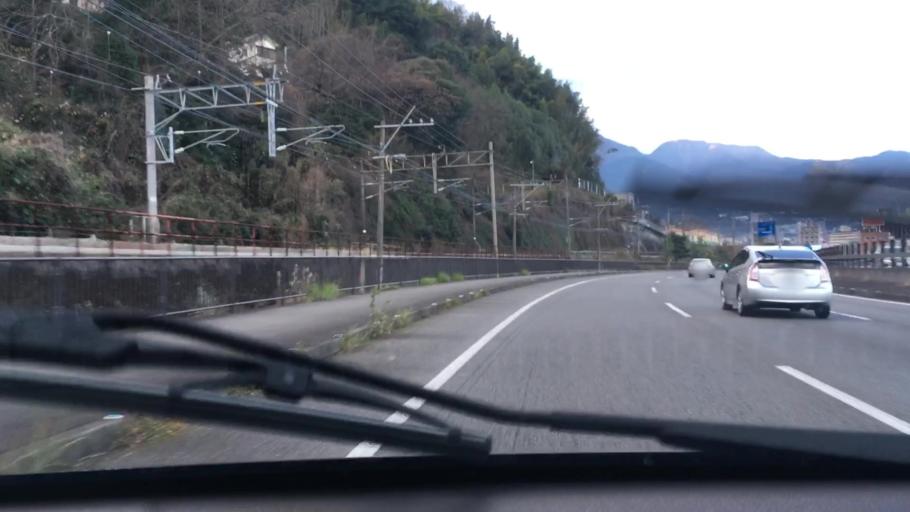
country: JP
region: Oita
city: Beppu
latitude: 33.2654
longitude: 131.5160
